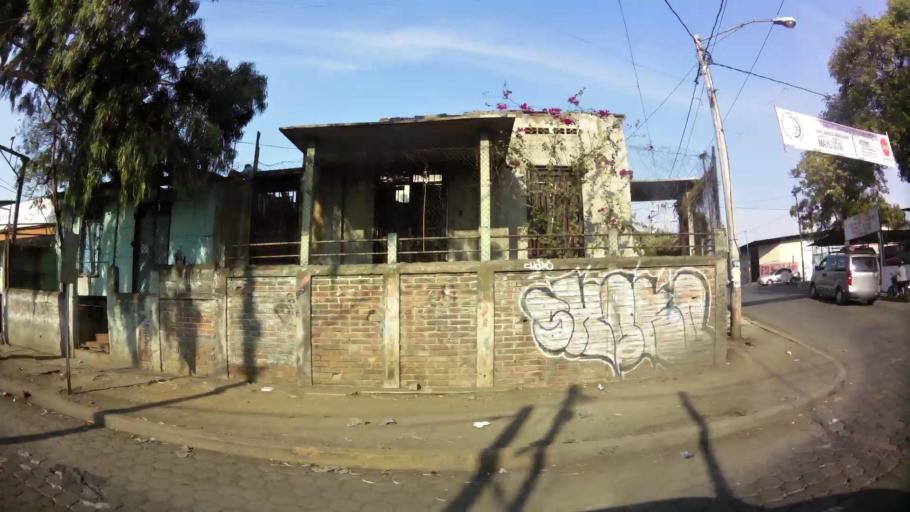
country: NI
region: Managua
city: Managua
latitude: 12.1437
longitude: -86.2600
